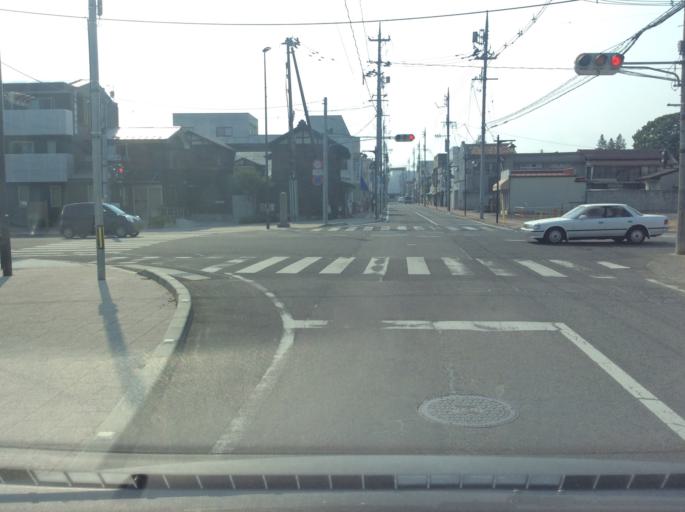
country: JP
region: Fukushima
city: Sukagawa
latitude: 37.1257
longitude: 140.2187
